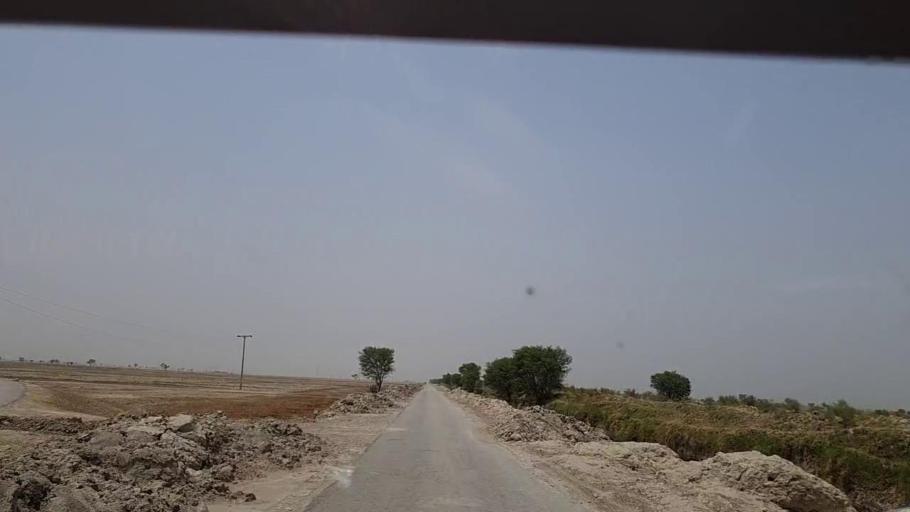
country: PK
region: Sindh
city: Khairpur Nathan Shah
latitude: 27.0181
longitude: 67.6219
